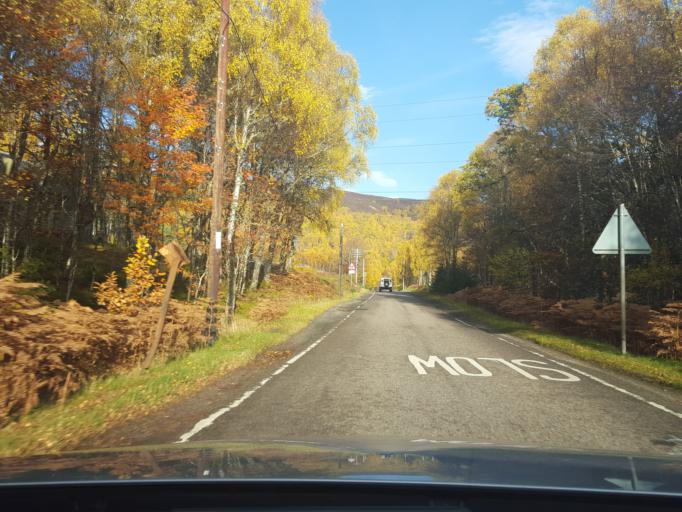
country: GB
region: Scotland
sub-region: Highland
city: Spean Bridge
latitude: 57.1784
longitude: -4.8002
